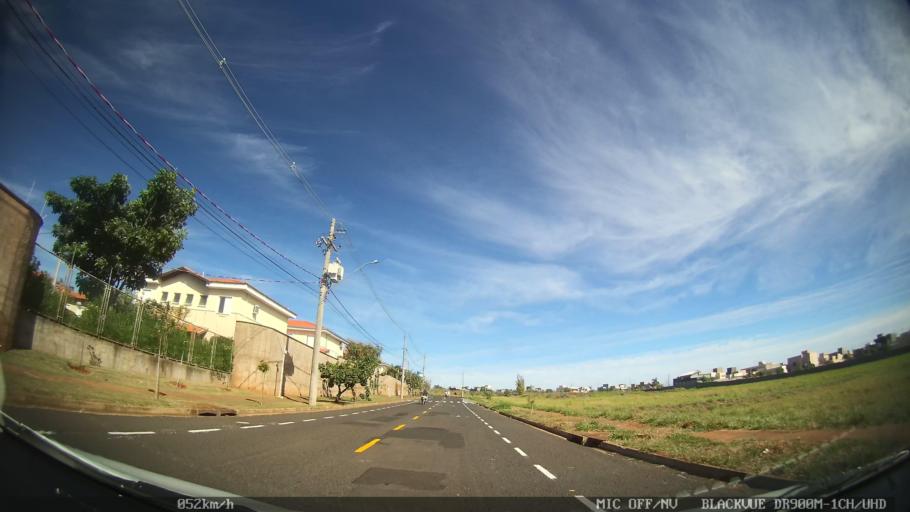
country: BR
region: Sao Paulo
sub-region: Sao Jose Do Rio Preto
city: Sao Jose do Rio Preto
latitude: -20.8035
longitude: -49.3325
